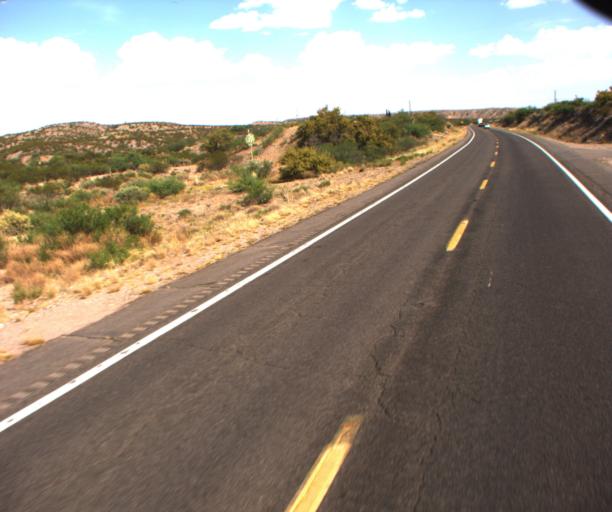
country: US
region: Arizona
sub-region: Greenlee County
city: Clifton
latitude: 32.8159
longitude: -109.1712
